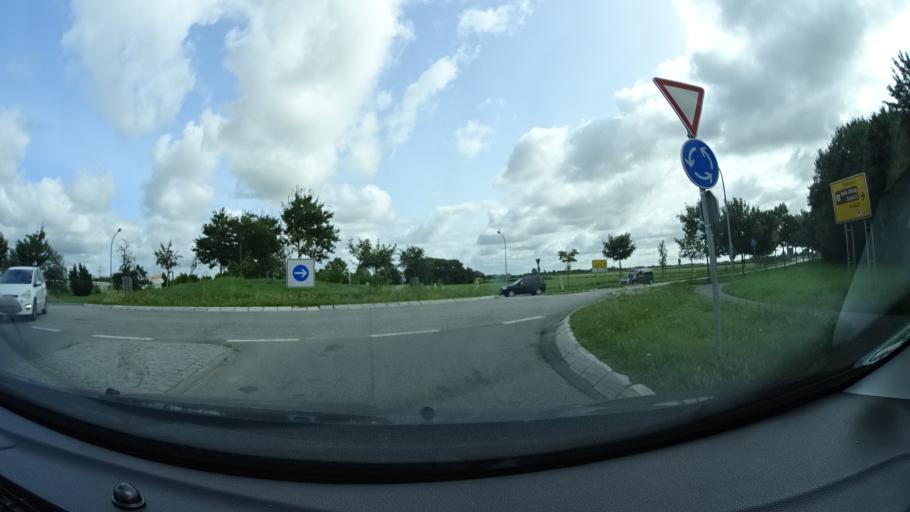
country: DE
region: Schleswig-Holstein
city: Bosbull
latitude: 54.7918
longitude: 8.8559
